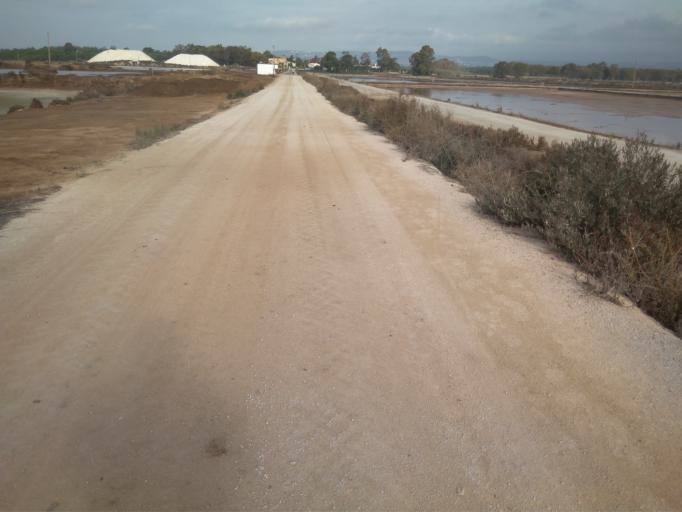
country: PT
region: Faro
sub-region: Faro
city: Faro
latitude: 37.0265
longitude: -7.9971
